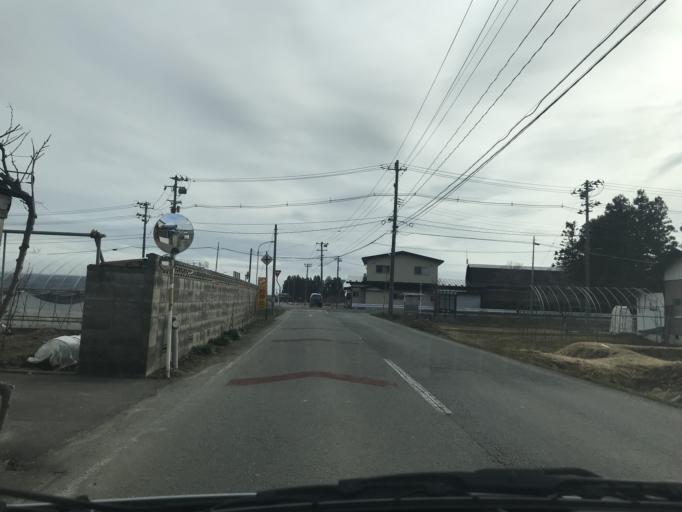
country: JP
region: Iwate
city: Hanamaki
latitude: 39.3992
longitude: 141.0751
